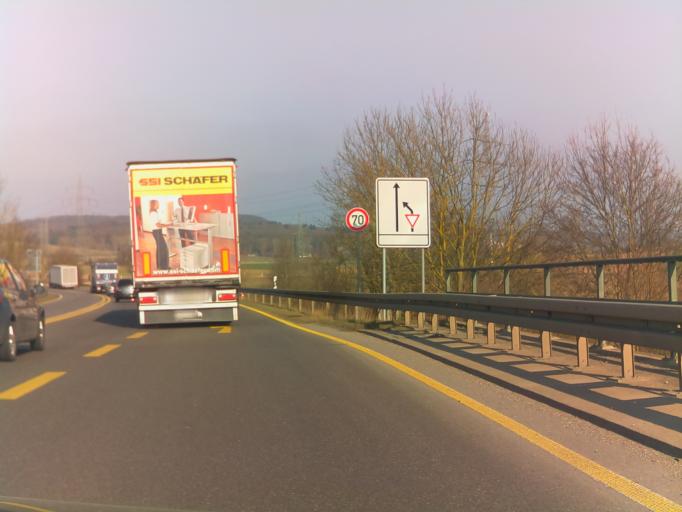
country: DE
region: Baden-Wuerttemberg
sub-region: Regierungsbezirk Stuttgart
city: Renningen
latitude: 48.7589
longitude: 8.9436
